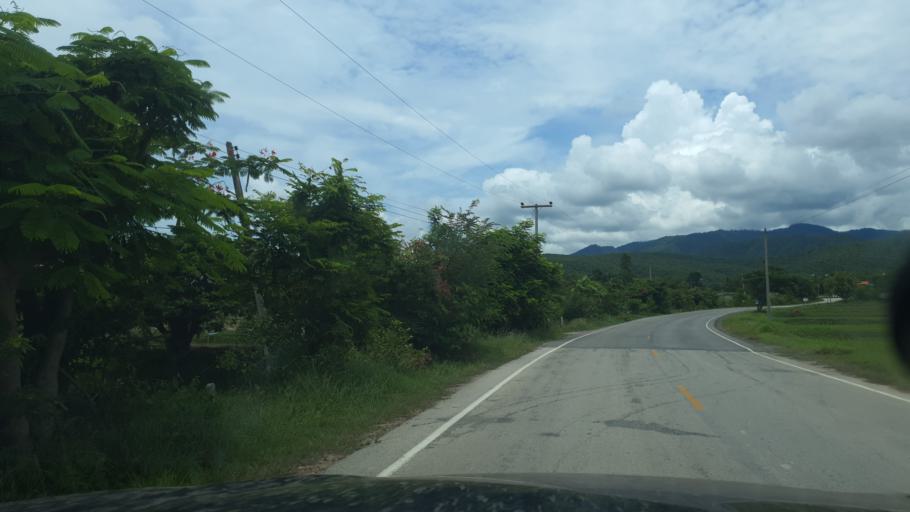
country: TH
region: Lampang
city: Sop Prap
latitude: 17.9212
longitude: 99.4081
